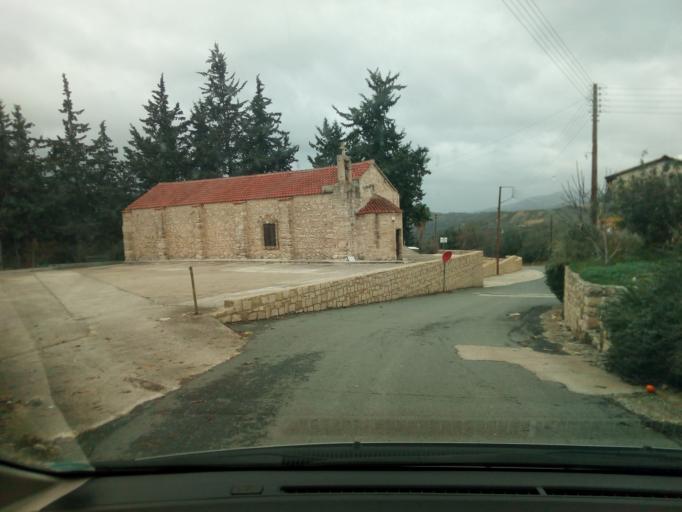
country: CY
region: Pafos
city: Tala
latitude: 34.9262
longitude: 32.4729
